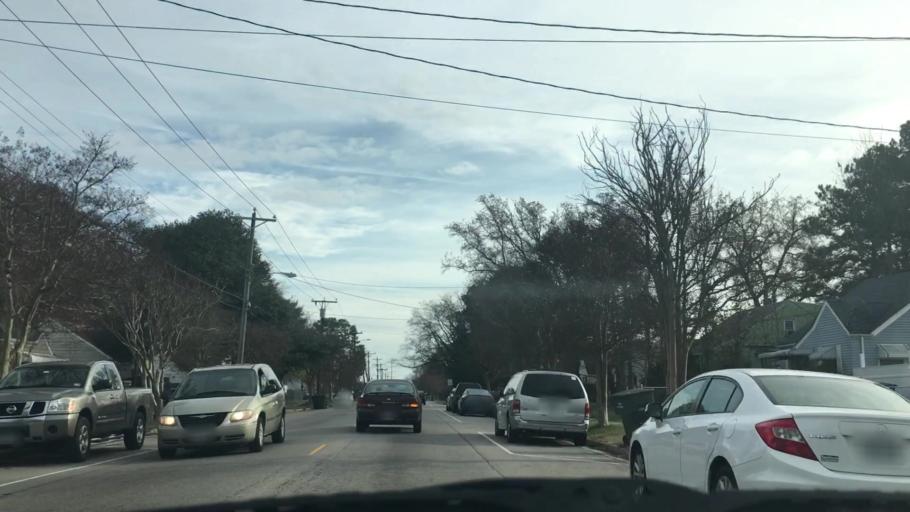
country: US
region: Virginia
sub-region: City of Norfolk
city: Norfolk
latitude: 36.8834
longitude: -76.2573
